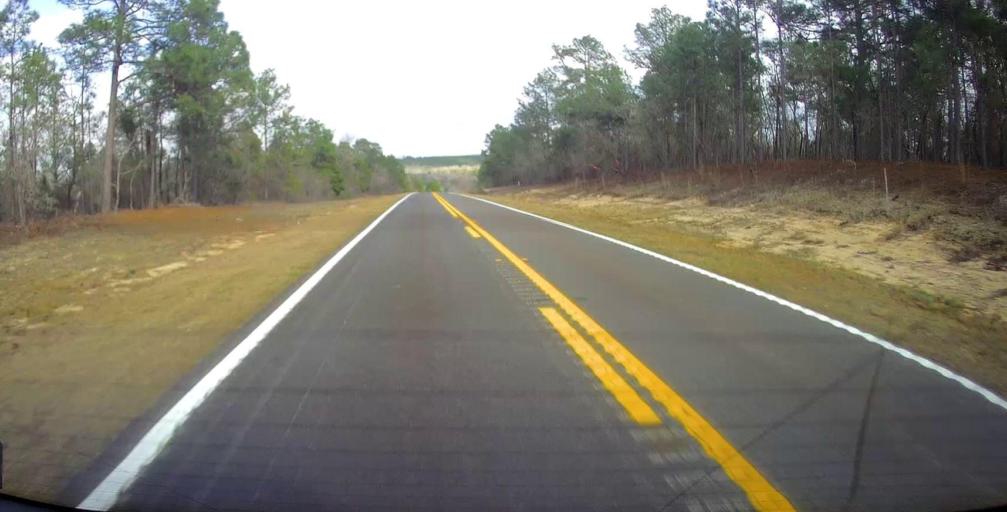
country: US
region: Georgia
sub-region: Marion County
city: Buena Vista
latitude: 32.4397
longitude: -84.4959
